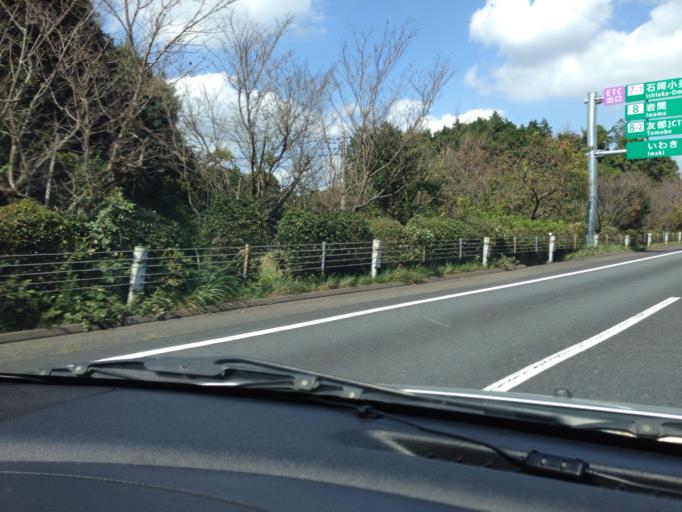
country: JP
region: Ibaraki
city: Ishioka
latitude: 36.1943
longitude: 140.2592
